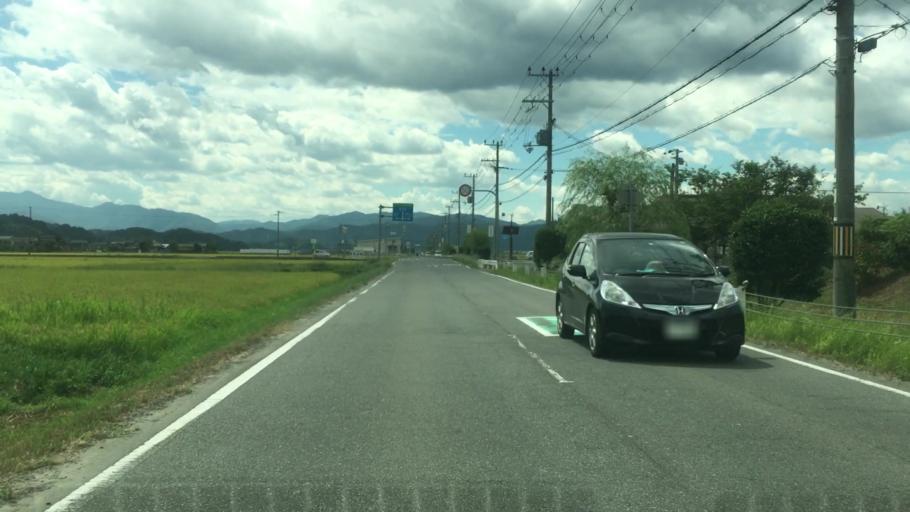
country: JP
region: Hyogo
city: Toyooka
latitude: 35.5294
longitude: 134.8398
